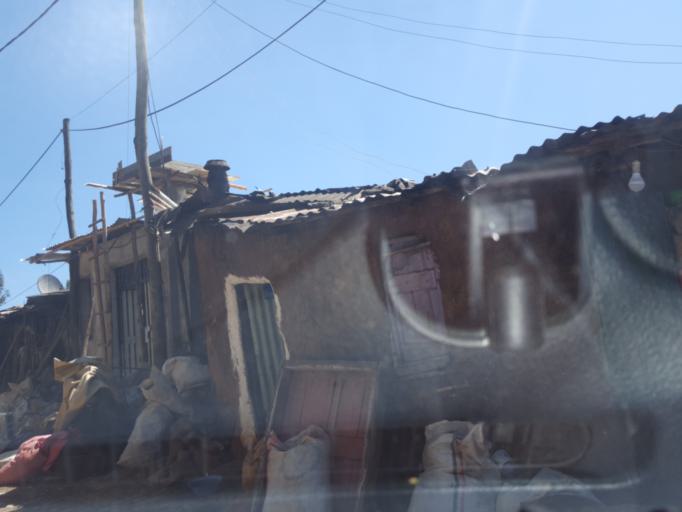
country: ET
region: Adis Abeba
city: Addis Ababa
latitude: 9.0587
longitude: 38.7480
